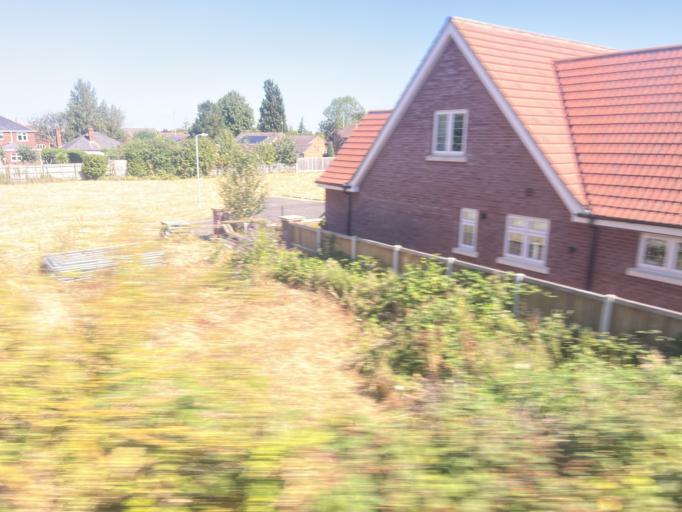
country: GB
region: England
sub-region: Lincolnshire
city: Boston
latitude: 52.9719
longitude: -0.0563
